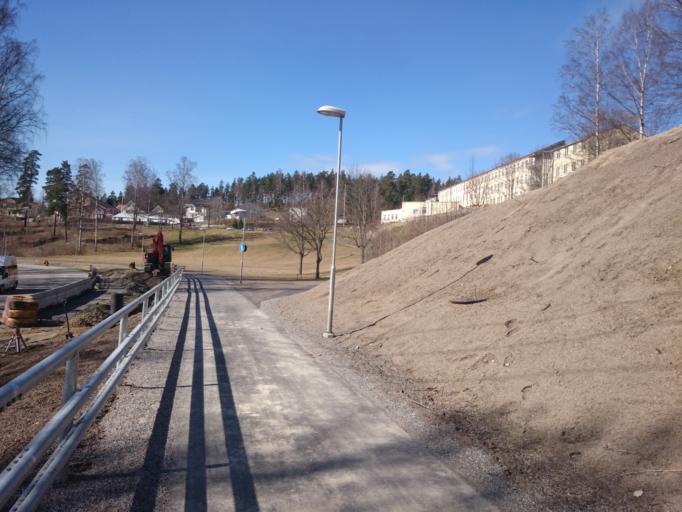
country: SE
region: Stockholm
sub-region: Botkyrka Kommun
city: Tumba
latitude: 59.2008
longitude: 17.8068
